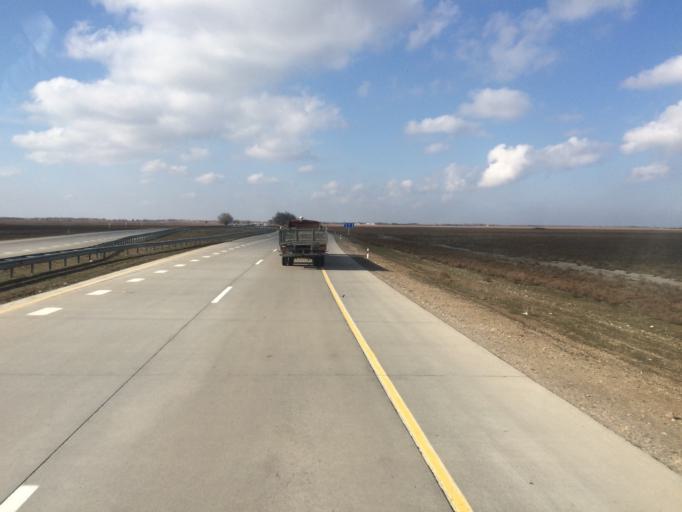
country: KZ
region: Ongtustik Qazaqstan
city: Temirlanovka
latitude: 42.8710
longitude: 69.0533
